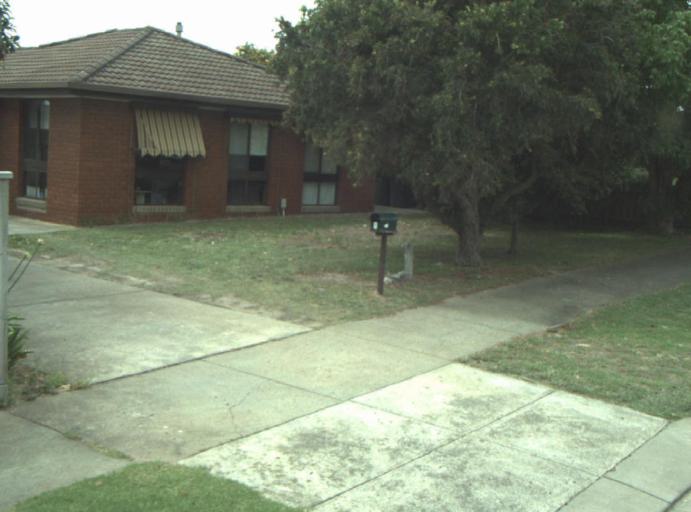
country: AU
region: Victoria
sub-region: Greater Geelong
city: Wandana Heights
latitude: -38.2041
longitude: 144.3238
